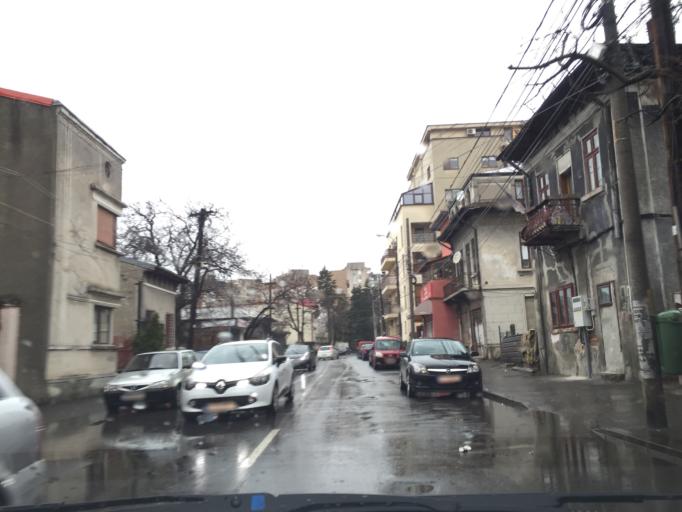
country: RO
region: Bucuresti
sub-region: Municipiul Bucuresti
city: Bucuresti
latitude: 44.4226
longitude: 26.0776
